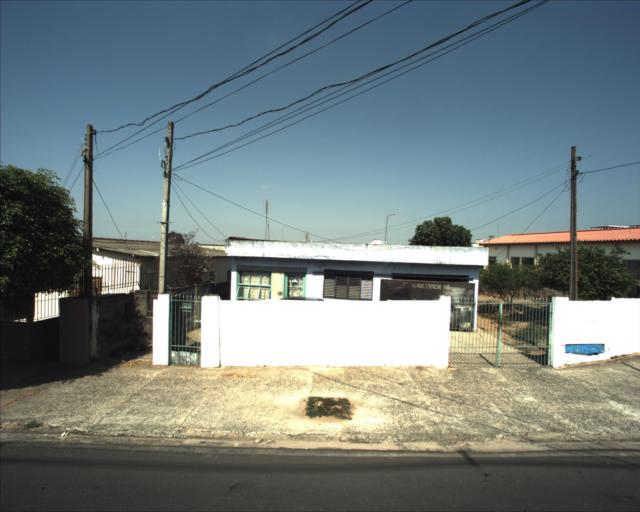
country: BR
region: Sao Paulo
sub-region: Sorocaba
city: Sorocaba
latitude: -23.4590
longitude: -47.4832
